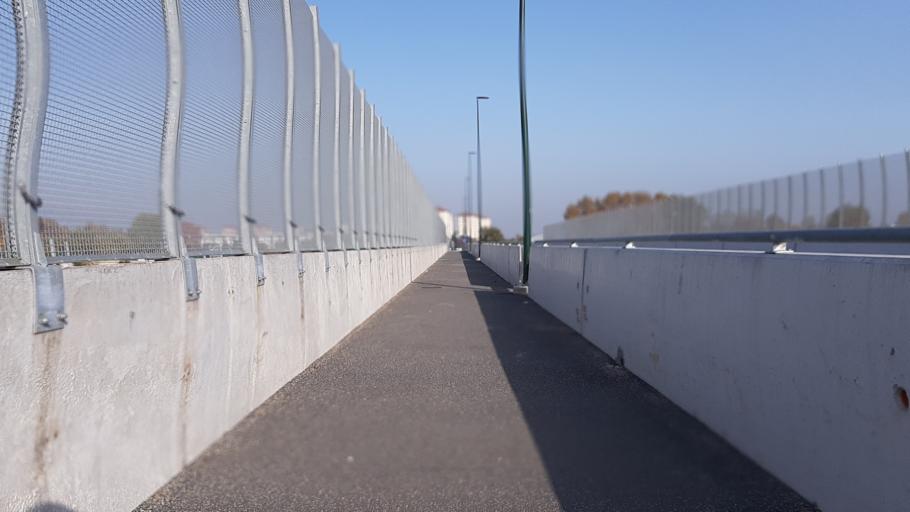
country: IT
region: Piedmont
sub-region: Provincia di Torino
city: Settimo Torinese
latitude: 45.1221
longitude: 7.7157
